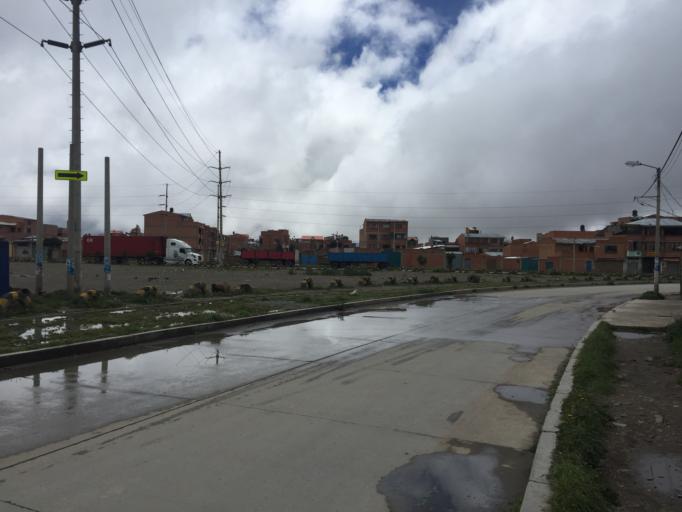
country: BO
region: La Paz
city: La Paz
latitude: -16.5257
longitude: -68.1641
